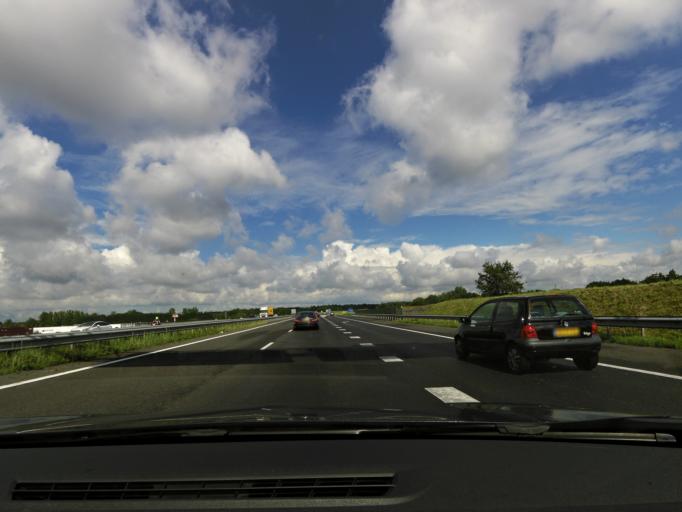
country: NL
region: North Brabant
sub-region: Gemeente Bergen op Zoom
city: Bergen op Zoom
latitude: 51.5051
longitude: 4.3118
